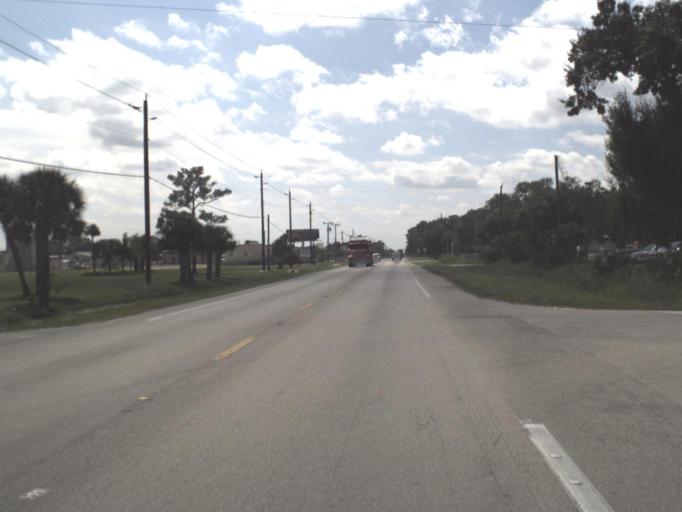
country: US
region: Florida
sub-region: Hendry County
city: LaBelle
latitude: 26.7434
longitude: -81.4379
